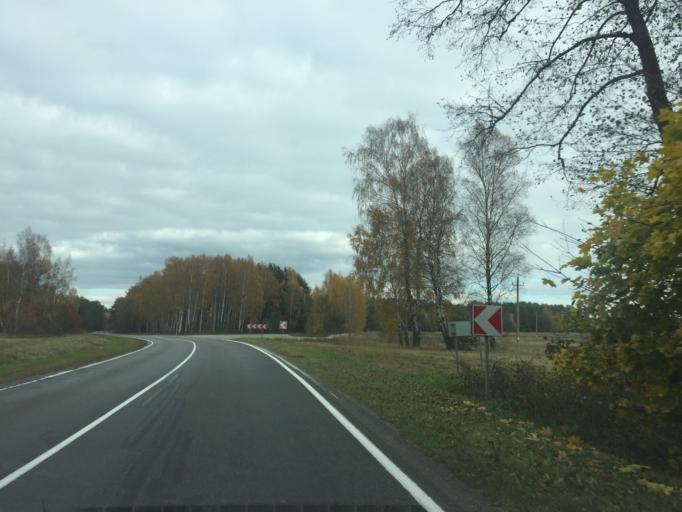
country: BY
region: Minsk
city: Svir
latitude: 54.8802
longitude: 26.3685
